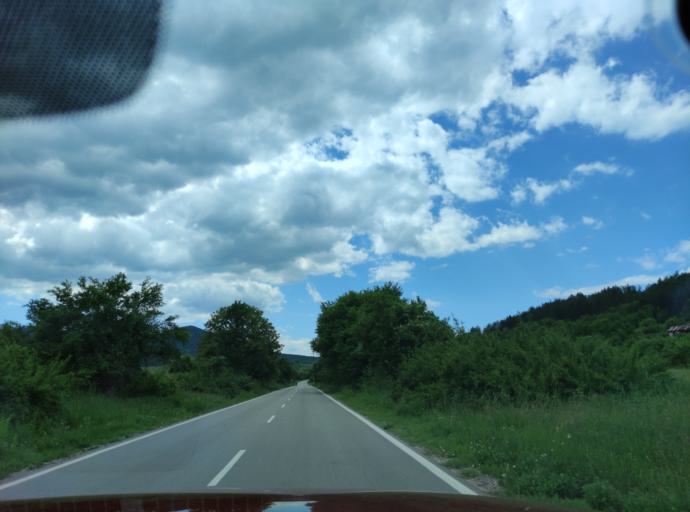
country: BG
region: Montana
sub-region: Obshtina Chiprovtsi
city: Chiprovtsi
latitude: 43.4482
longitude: 22.9158
